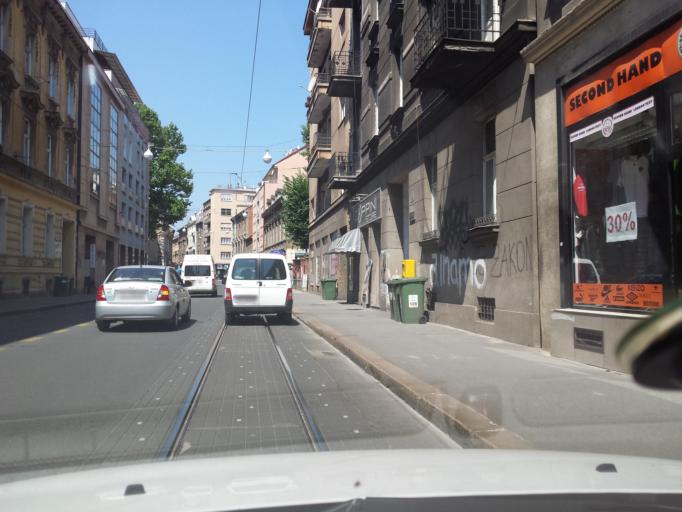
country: HR
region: Grad Zagreb
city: Zagreb - Centar
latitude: 45.8129
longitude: 15.9604
